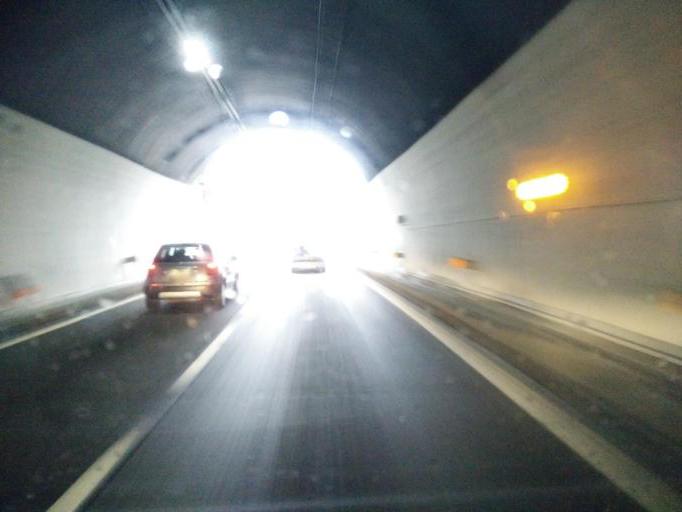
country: IT
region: Tuscany
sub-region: Province of Florence
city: Barberino di Mugello
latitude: 44.0798
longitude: 11.2304
